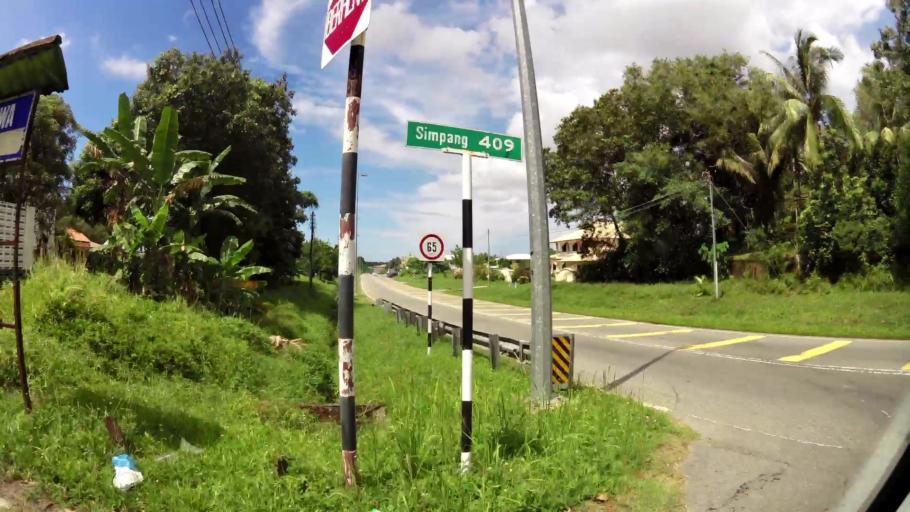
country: BN
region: Brunei and Muara
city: Bandar Seri Begawan
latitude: 4.9786
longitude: 114.9487
